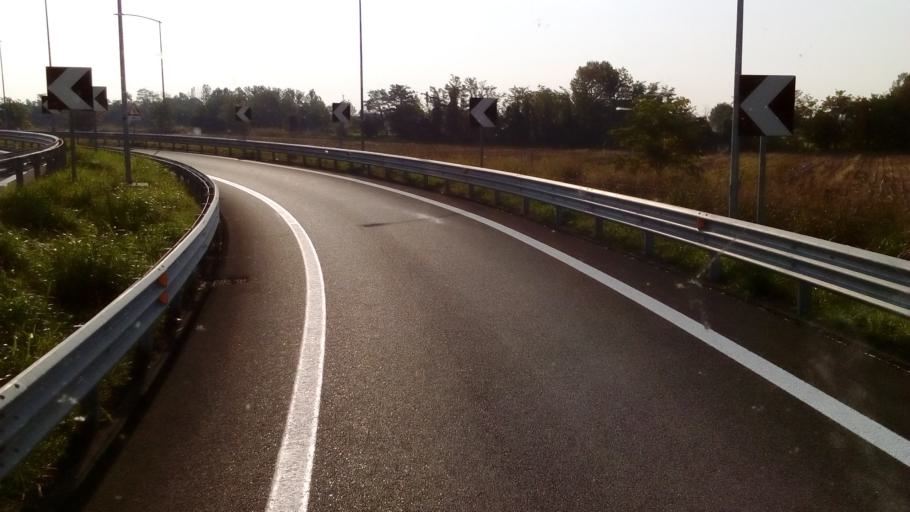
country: IT
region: Lombardy
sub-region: Provincia di Bergamo
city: Casirate d'Adda
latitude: 45.5061
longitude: 9.5508
